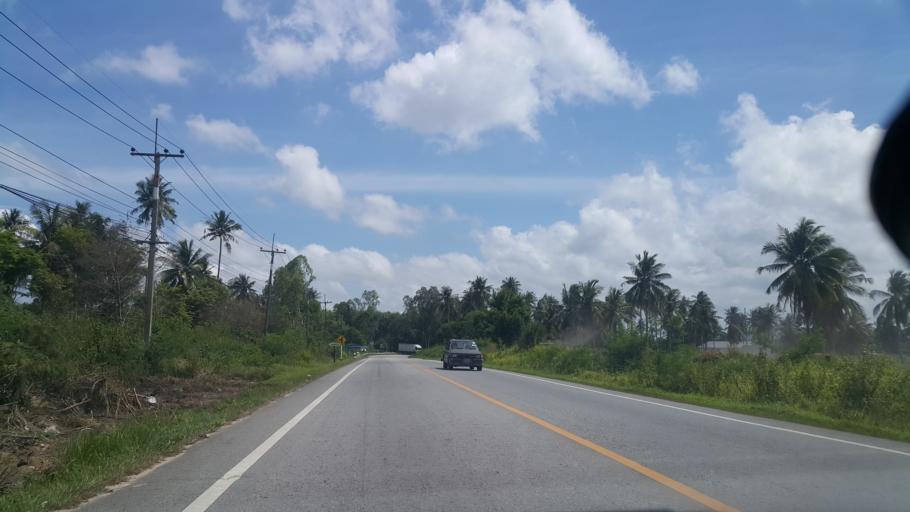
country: TH
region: Rayong
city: Ban Chang
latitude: 12.7980
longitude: 101.0504
